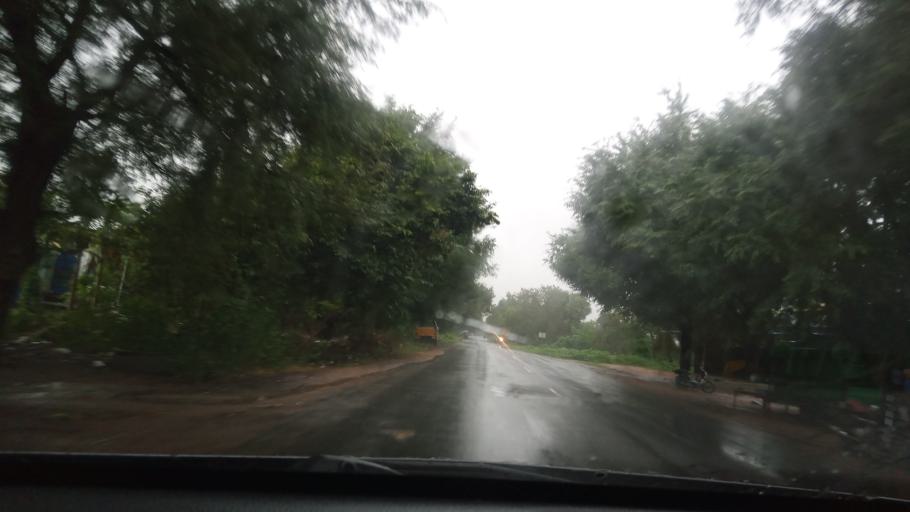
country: IN
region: Tamil Nadu
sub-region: Vellore
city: Walajapet
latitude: 12.8497
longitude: 79.3899
